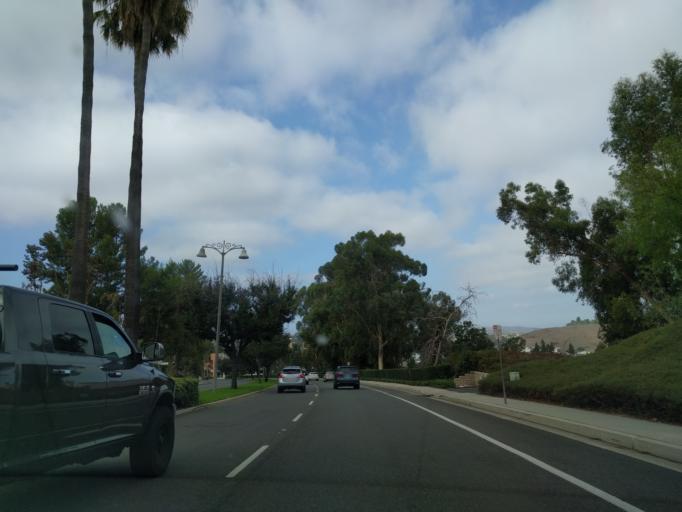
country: US
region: California
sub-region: Orange County
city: Ladera Ranch
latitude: 33.5578
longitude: -117.6659
